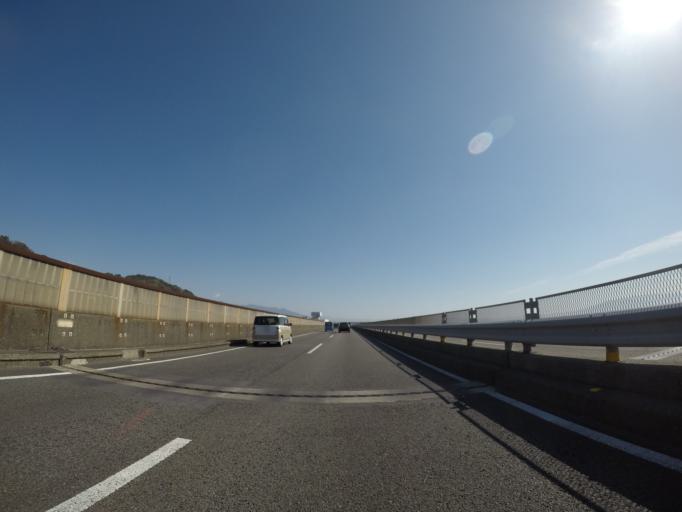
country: JP
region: Shizuoka
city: Fuji
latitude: 35.1147
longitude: 138.5981
